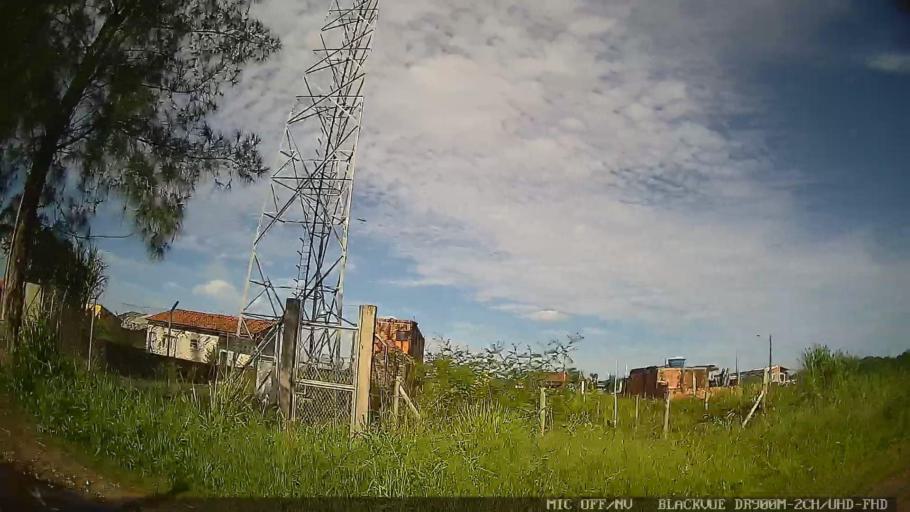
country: BR
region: Sao Paulo
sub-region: Iguape
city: Iguape
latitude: -24.7654
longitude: -47.5817
